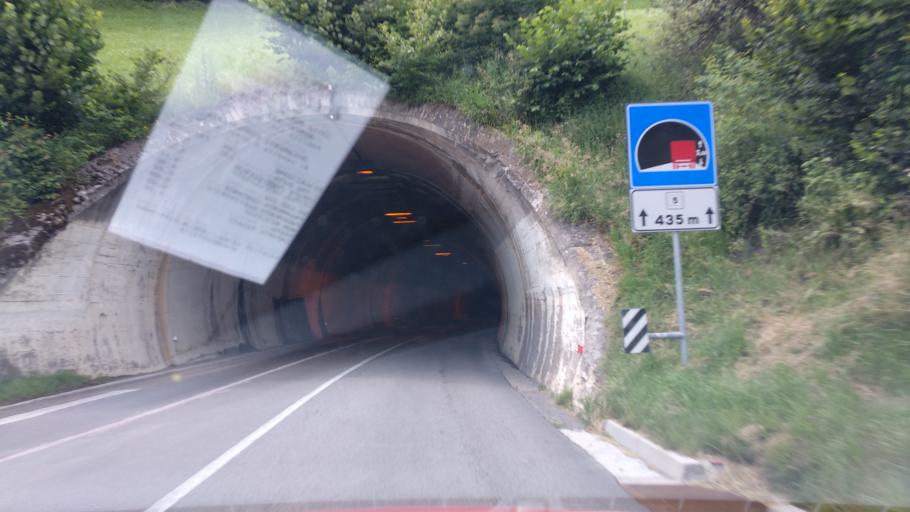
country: IT
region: Trentino-Alto Adige
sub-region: Bolzano
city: Avelengo
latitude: 46.6456
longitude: 11.2104
